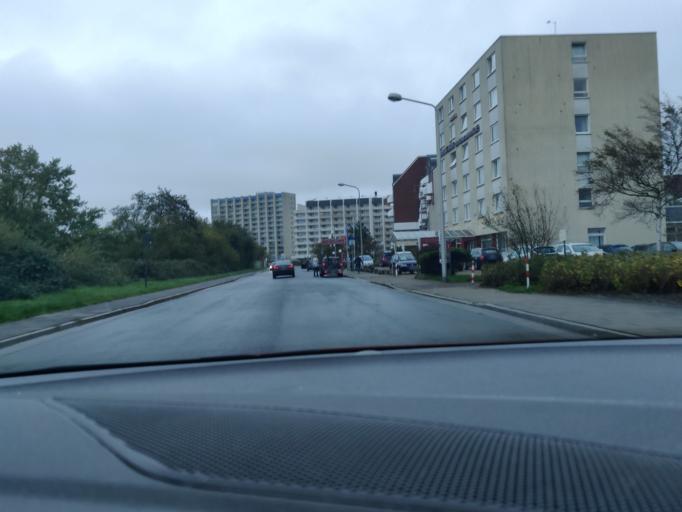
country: DE
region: Lower Saxony
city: Cuxhaven
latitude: 53.8890
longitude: 8.6678
